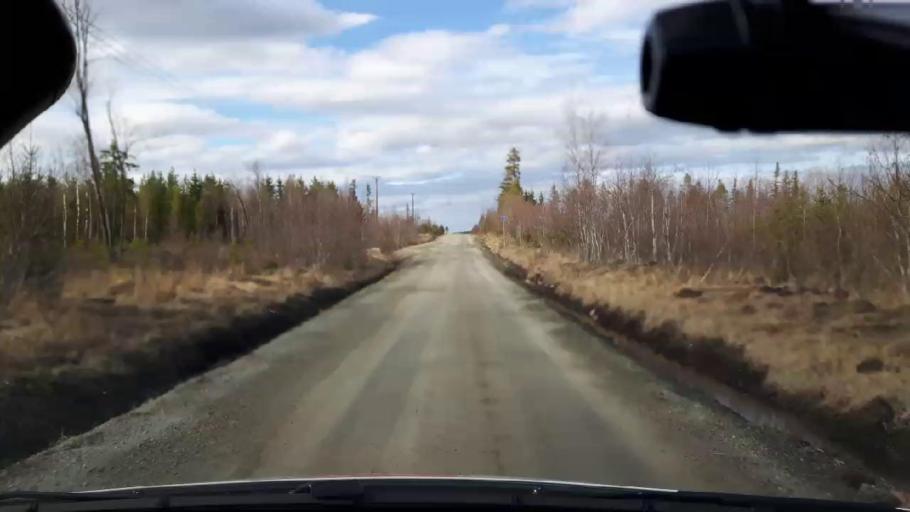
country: SE
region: Jaemtland
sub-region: Bergs Kommun
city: Hoverberg
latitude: 62.8380
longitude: 14.6664
